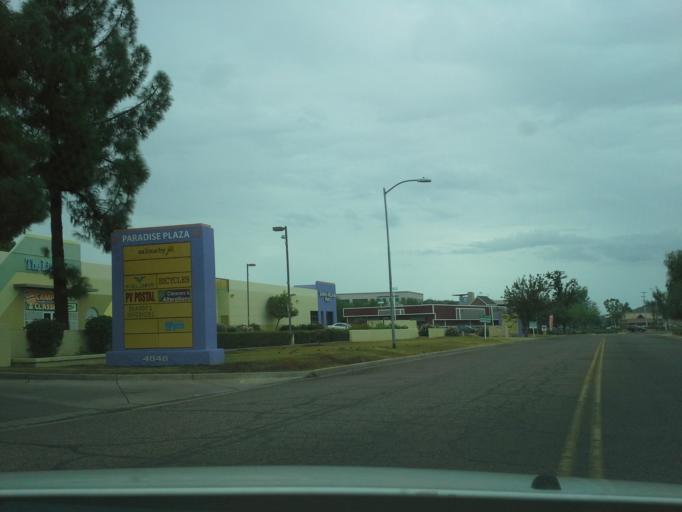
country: US
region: Arizona
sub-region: Maricopa County
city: Paradise Valley
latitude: 33.5997
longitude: -111.9779
